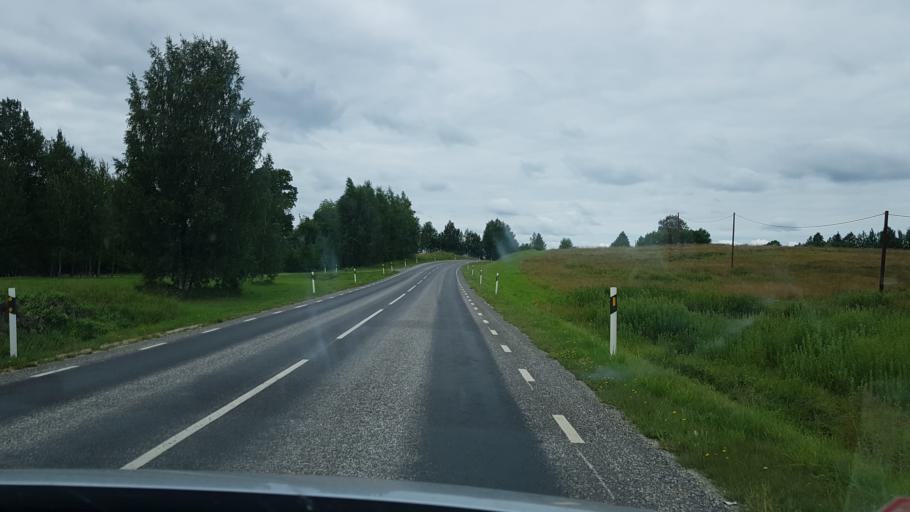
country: EE
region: Vorumaa
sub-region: Antsla vald
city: Vana-Antsla
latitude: 58.0058
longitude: 26.6142
